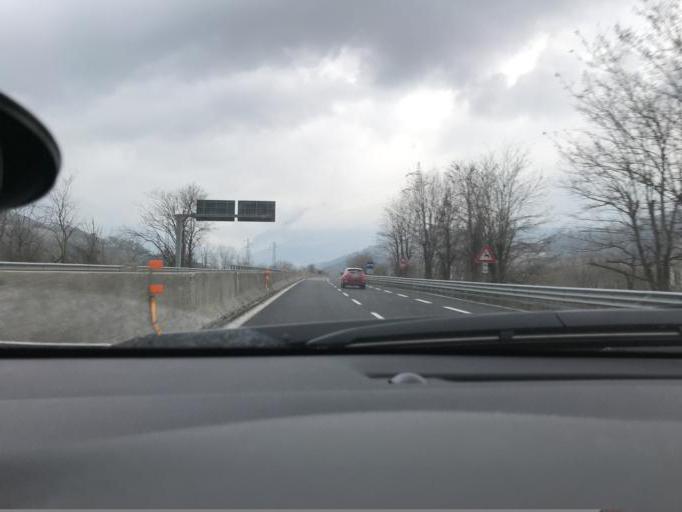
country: IT
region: The Marches
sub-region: Provincia di Ancona
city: Rosora
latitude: 43.4647
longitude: 13.0645
